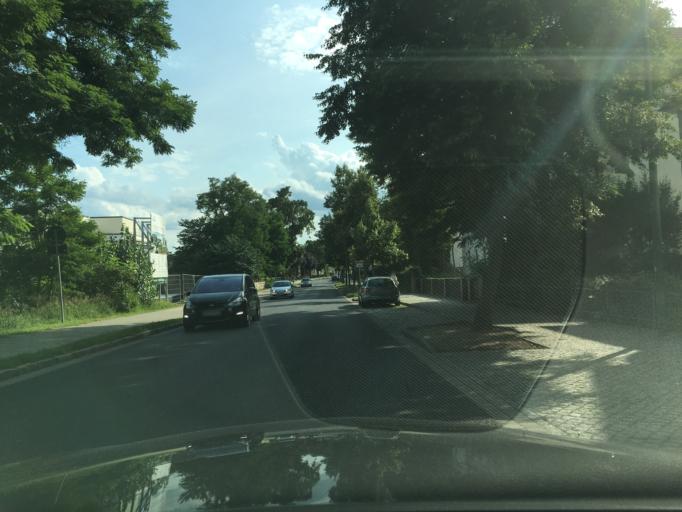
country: DE
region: Mecklenburg-Vorpommern
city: Neustrelitz
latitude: 53.3688
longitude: 13.0701
